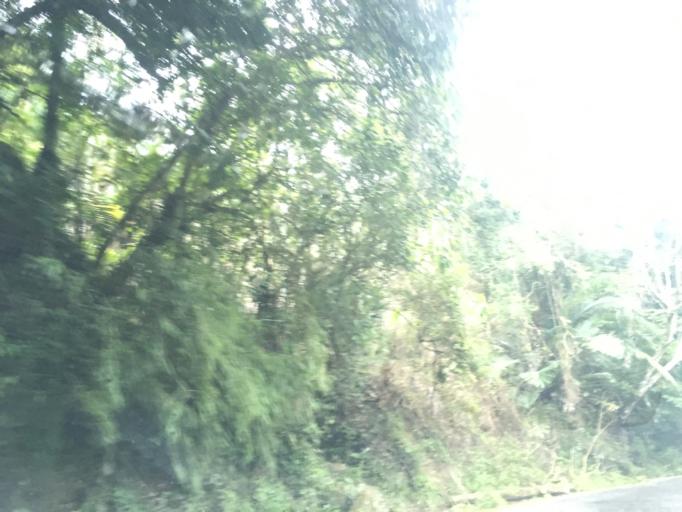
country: TW
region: Taiwan
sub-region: Yunlin
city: Douliu
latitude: 23.5712
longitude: 120.6424
